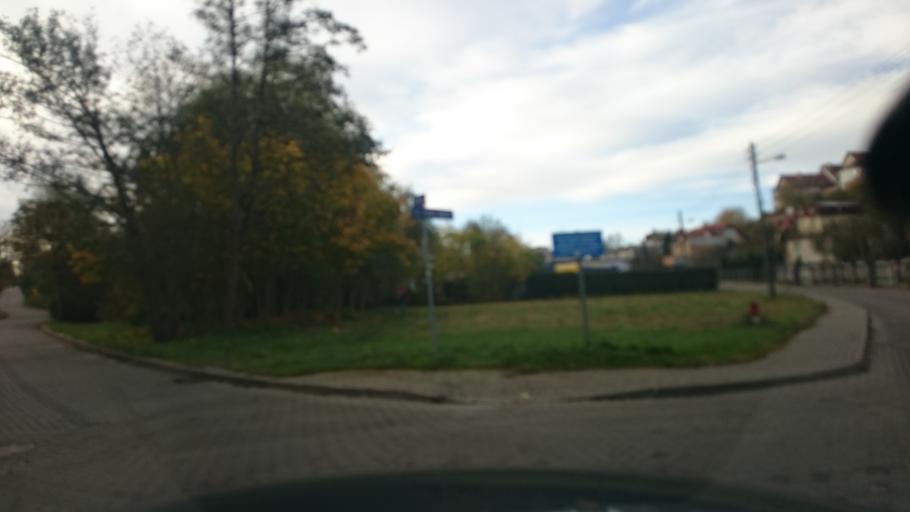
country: PL
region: Pomeranian Voivodeship
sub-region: Gdynia
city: Wielki Kack
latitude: 54.4675
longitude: 18.4929
